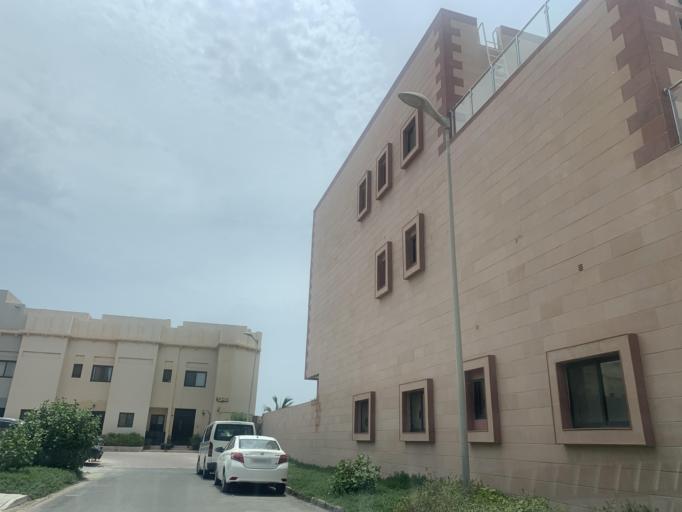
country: BH
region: Muharraq
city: Al Hadd
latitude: 26.2926
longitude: 50.6700
